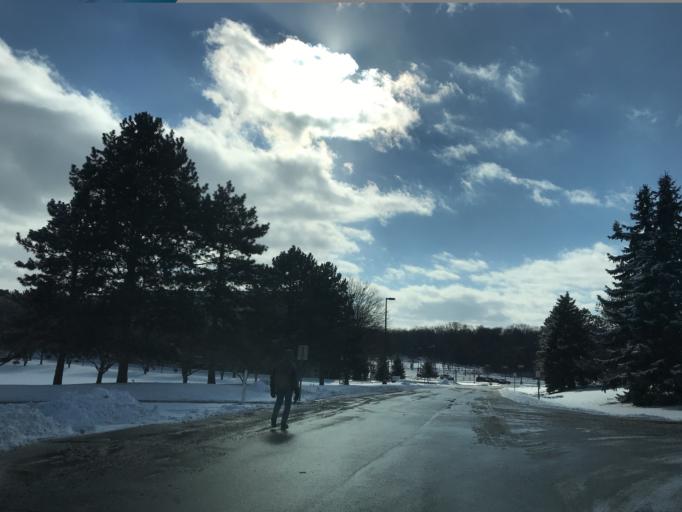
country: US
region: Michigan
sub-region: Washtenaw County
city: Ypsilanti
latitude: 42.2650
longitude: -83.6674
